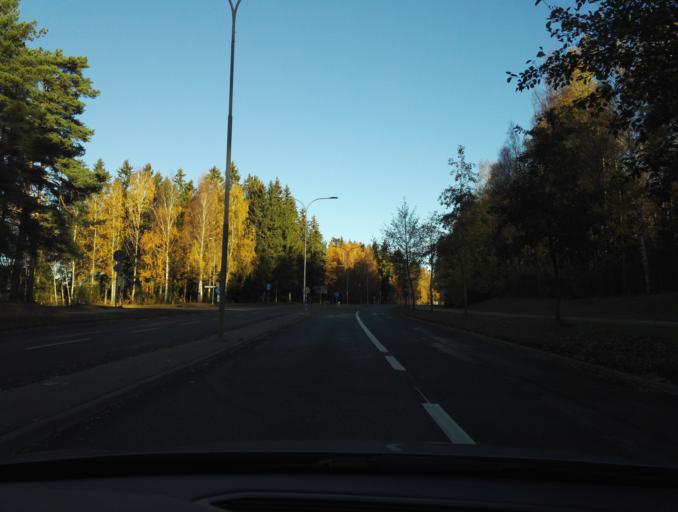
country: SE
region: Kronoberg
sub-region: Vaxjo Kommun
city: Vaexjoe
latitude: 56.8973
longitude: 14.7805
